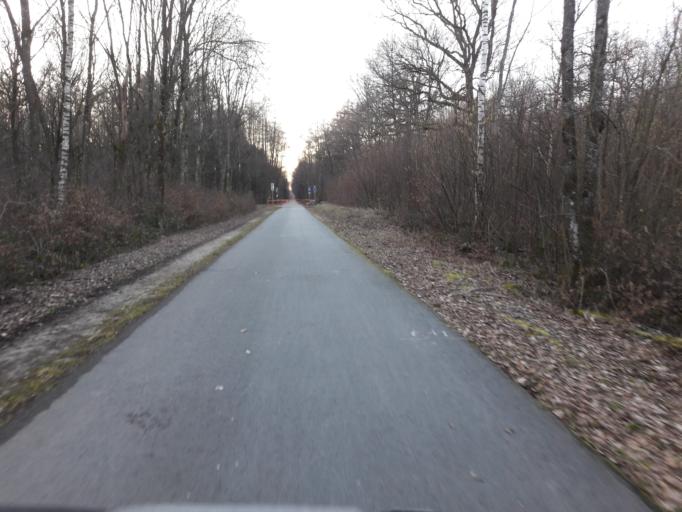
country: BE
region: Wallonia
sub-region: Province du Hainaut
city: Momignies
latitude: 50.0255
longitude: 4.2034
